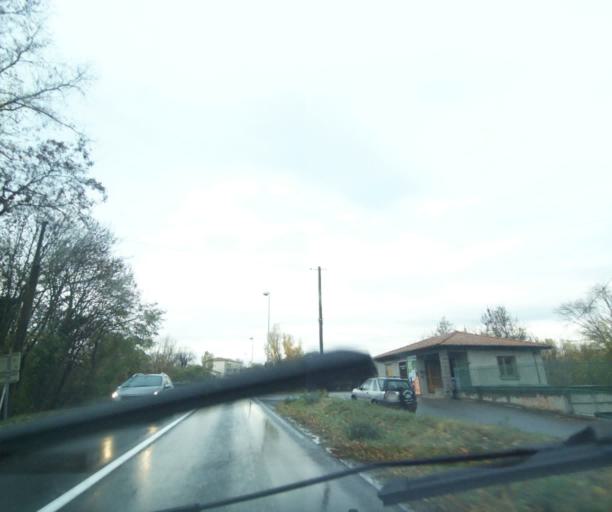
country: FR
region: Auvergne
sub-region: Departement du Puy-de-Dome
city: Cournon-d'Auvergne
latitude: 45.7293
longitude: 3.2140
